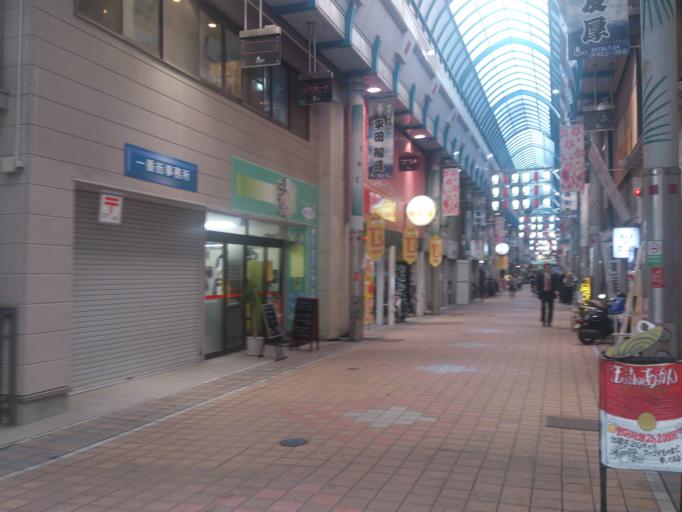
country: JP
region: Kagoshima
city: Kagoshima-shi
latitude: 31.5820
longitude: 130.5428
